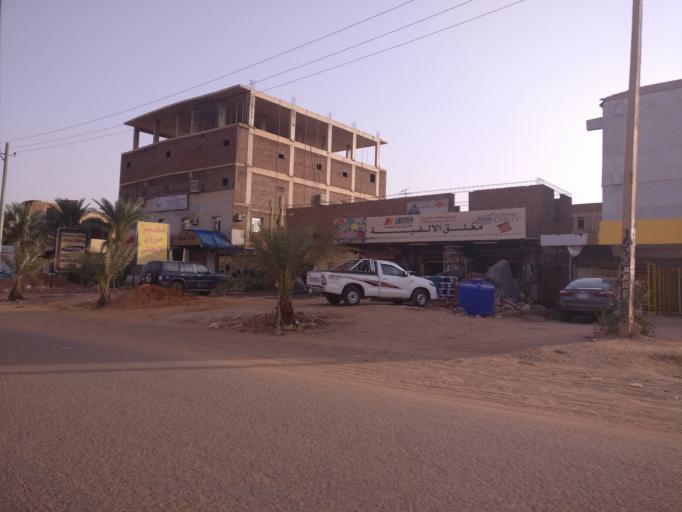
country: SD
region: Khartoum
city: Khartoum
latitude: 15.5391
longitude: 32.5674
